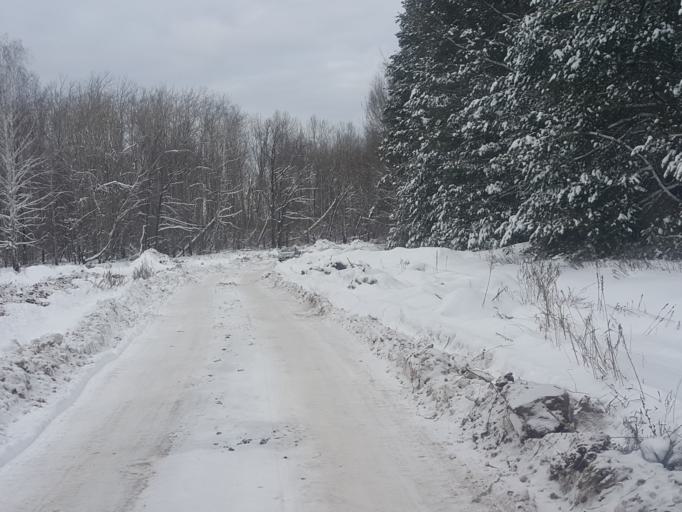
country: RU
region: Tambov
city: Platonovka
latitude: 52.8854
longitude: 41.8584
